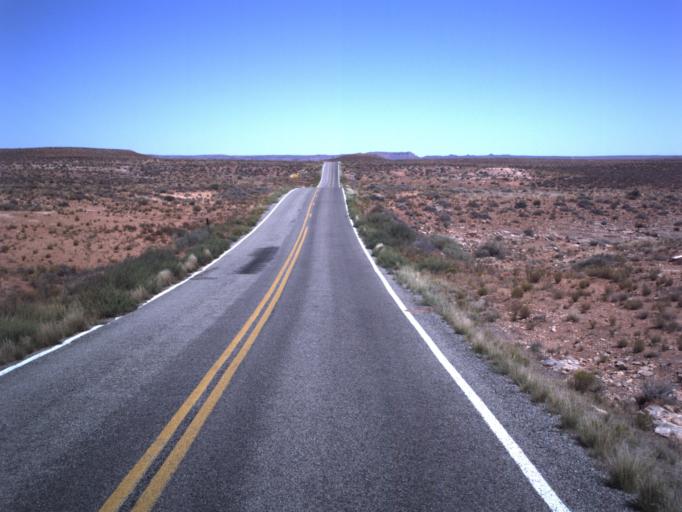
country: US
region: Arizona
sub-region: Navajo County
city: Kayenta
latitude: 37.1870
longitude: -109.9168
